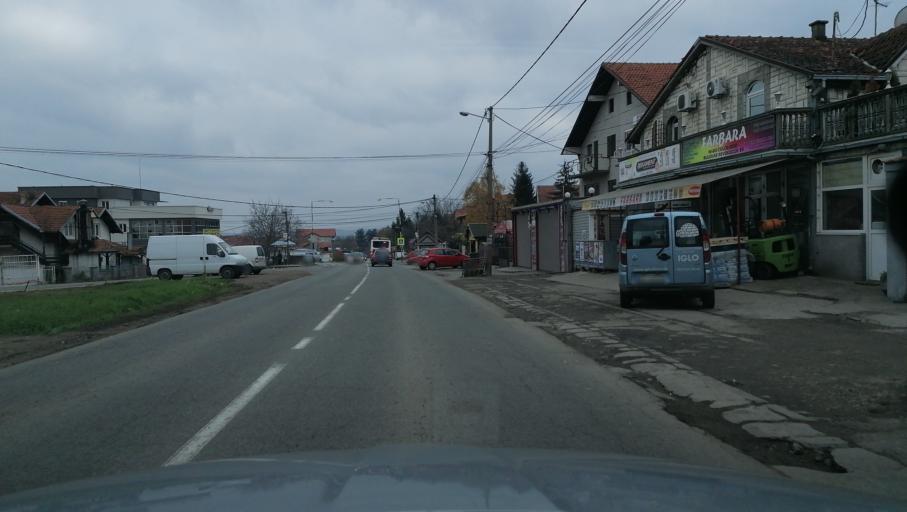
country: RS
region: Central Serbia
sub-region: Belgrade
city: Zvezdara
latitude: 44.7634
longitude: 20.5652
